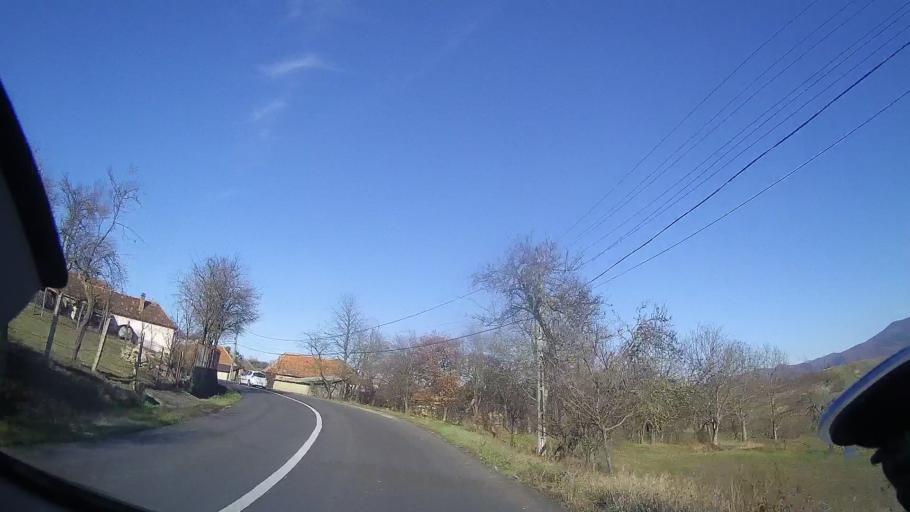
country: RO
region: Bihor
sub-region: Comuna Bratca
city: Beznea
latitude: 46.9659
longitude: 22.6160
